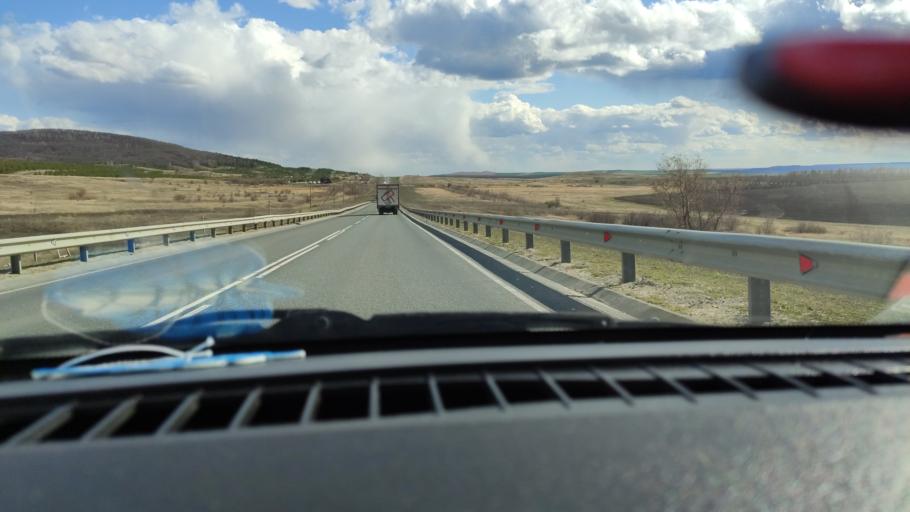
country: RU
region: Saratov
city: Alekseyevka
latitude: 52.3115
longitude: 47.9242
